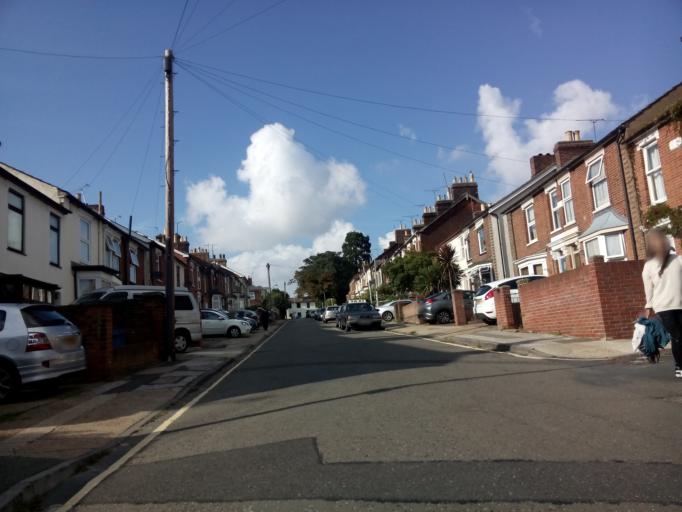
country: GB
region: England
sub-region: Suffolk
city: Ipswich
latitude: 52.0573
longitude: 1.1670
